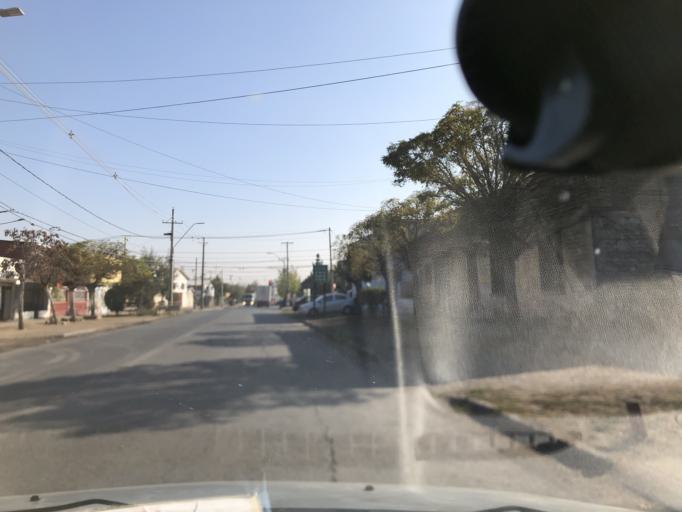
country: CL
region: Santiago Metropolitan
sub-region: Provincia de Cordillera
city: Puente Alto
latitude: -33.6193
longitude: -70.5849
